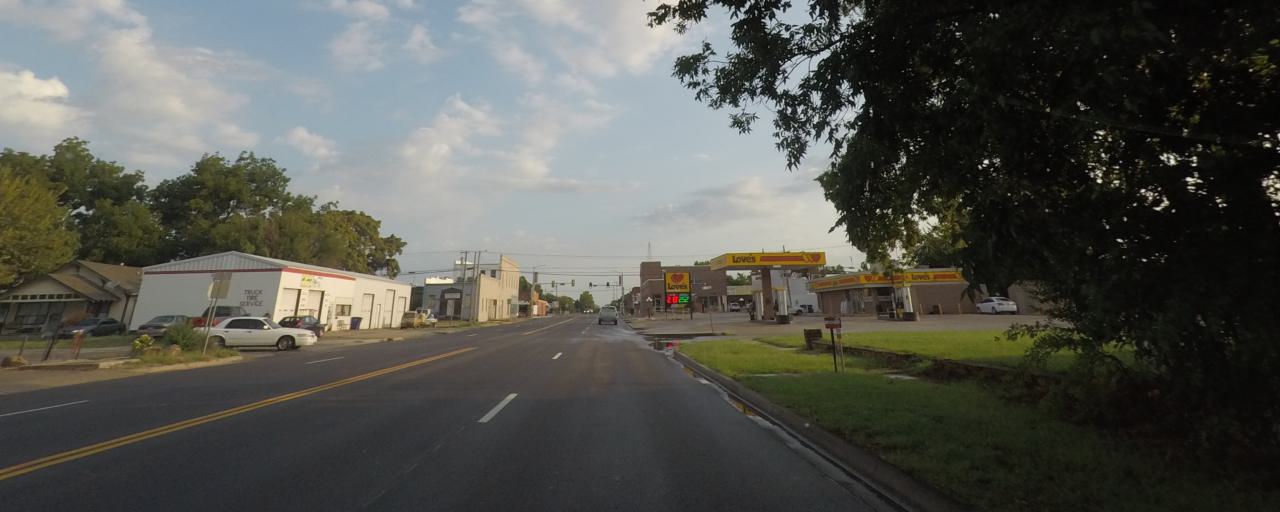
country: US
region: Oklahoma
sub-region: Stephens County
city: Comanche
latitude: 34.3676
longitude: -97.9642
